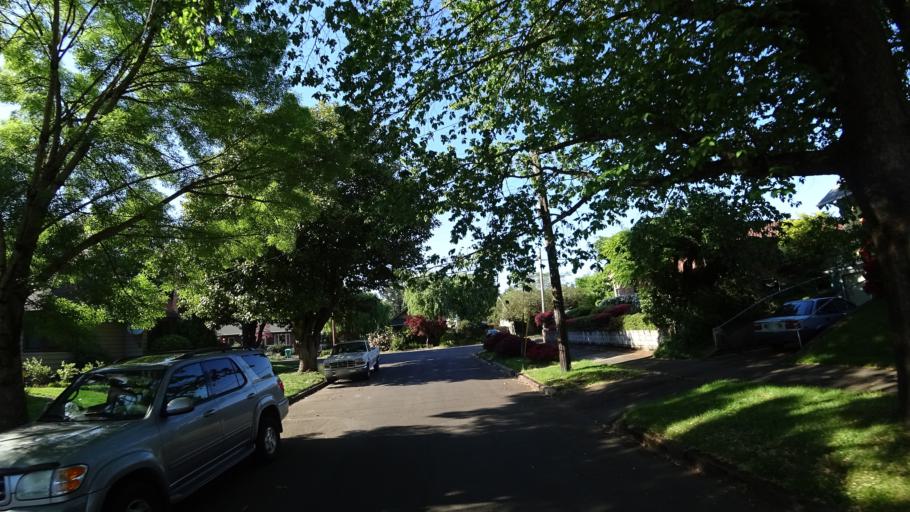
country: US
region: Oregon
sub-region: Multnomah County
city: Portland
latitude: 45.5544
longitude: -122.6871
